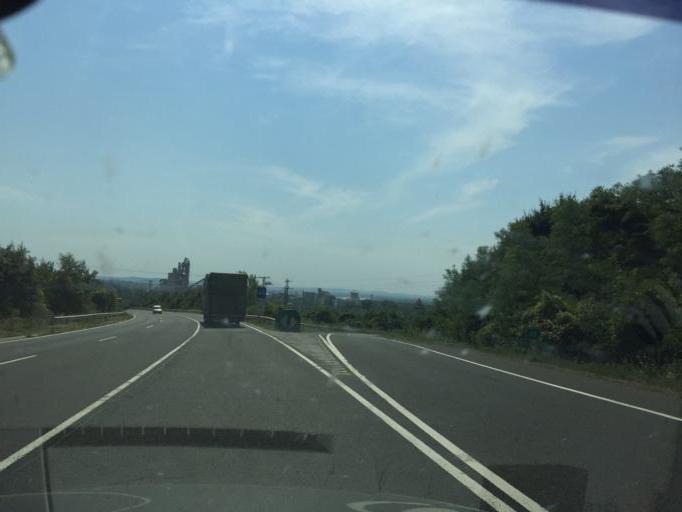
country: HU
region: Pest
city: Veroce
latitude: 47.8191
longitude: 19.0907
